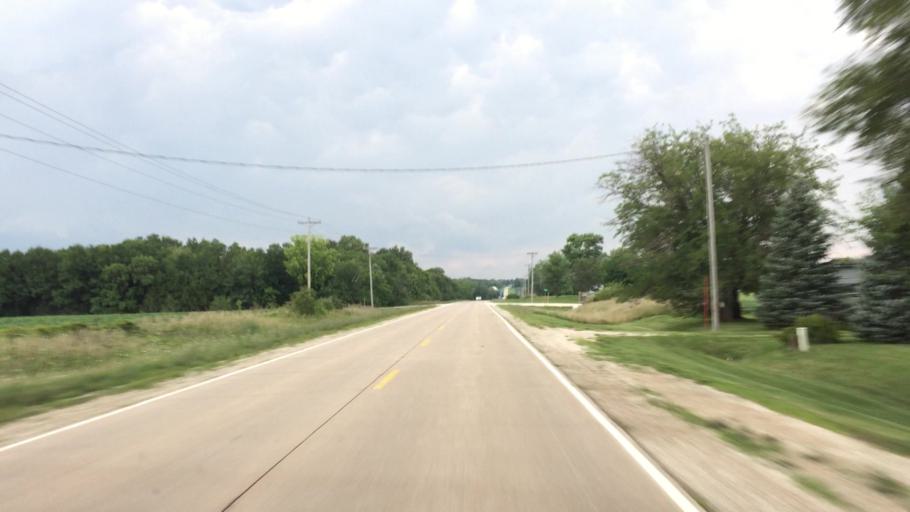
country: US
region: Iowa
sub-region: Lee County
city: Fort Madison
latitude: 40.7094
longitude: -91.3300
